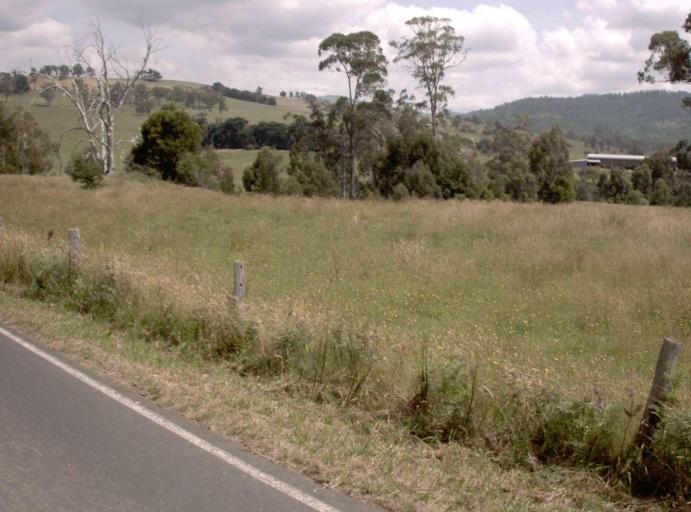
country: AU
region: Victoria
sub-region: Latrobe
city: Traralgon
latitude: -38.3030
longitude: 146.5394
